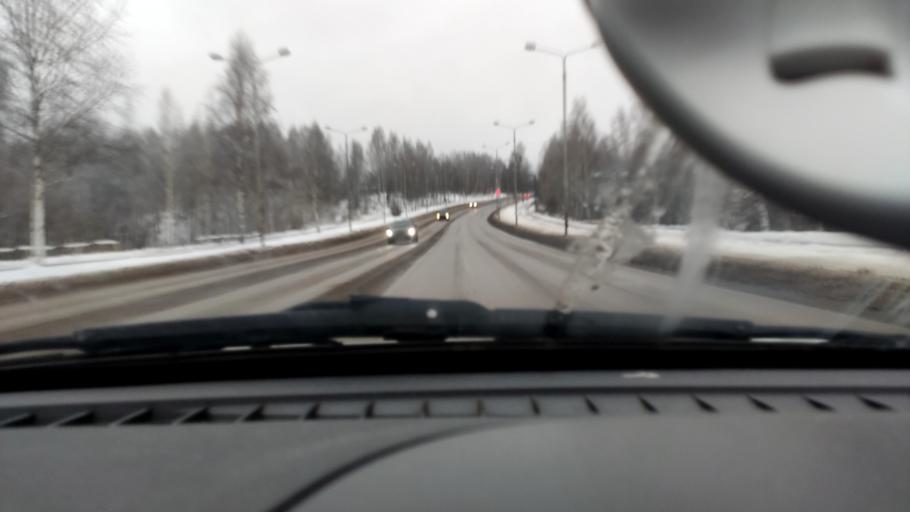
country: RU
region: Perm
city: Perm
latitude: 58.0959
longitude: 56.3847
